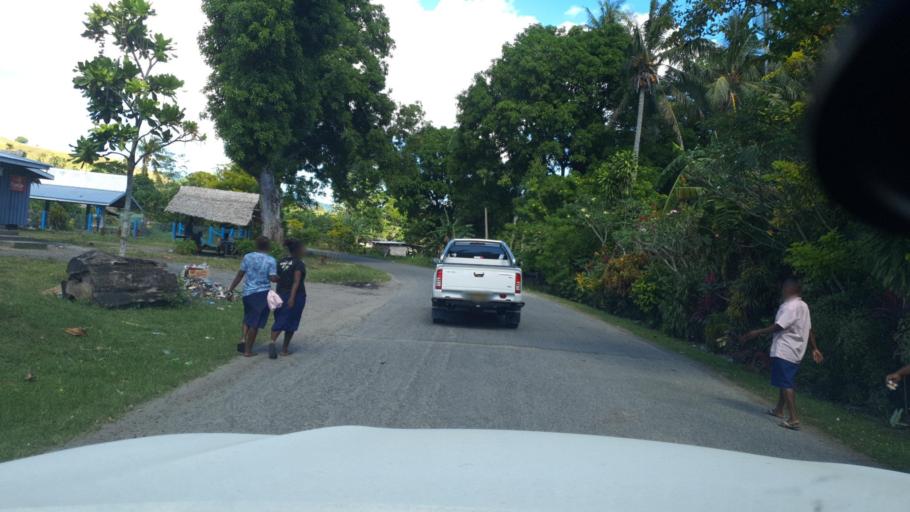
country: SB
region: Guadalcanal
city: Honiara
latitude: -9.2600
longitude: 159.6741
